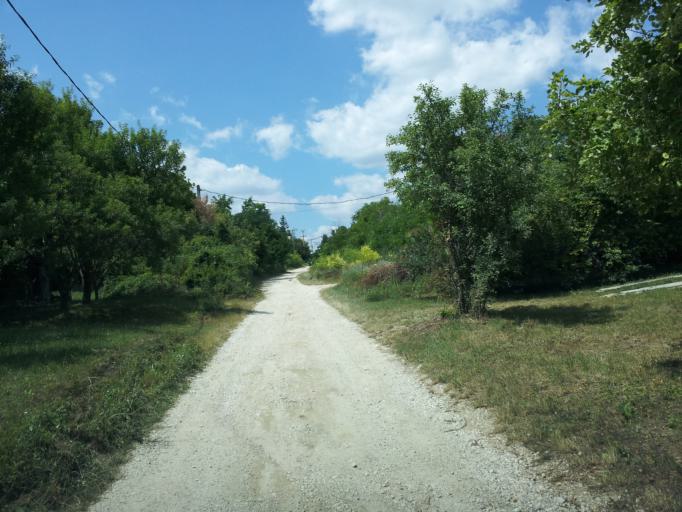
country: HU
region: Veszprem
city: Balatonkenese
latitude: 47.0403
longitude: 18.0940
